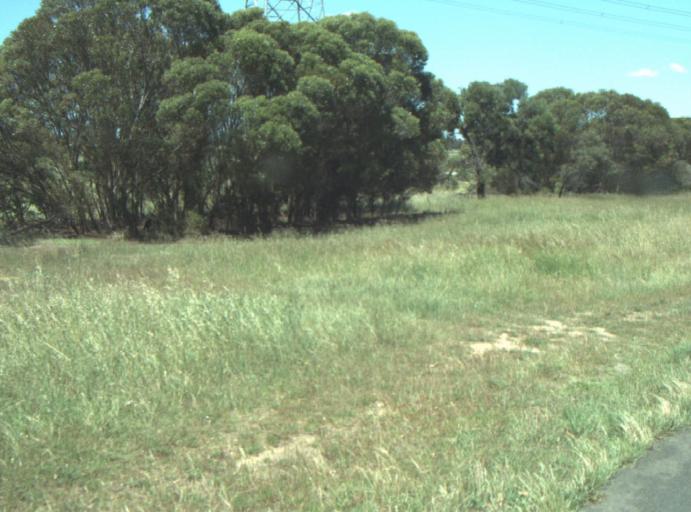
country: AU
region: Victoria
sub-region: Greater Geelong
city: Lara
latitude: -37.9056
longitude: 144.3702
